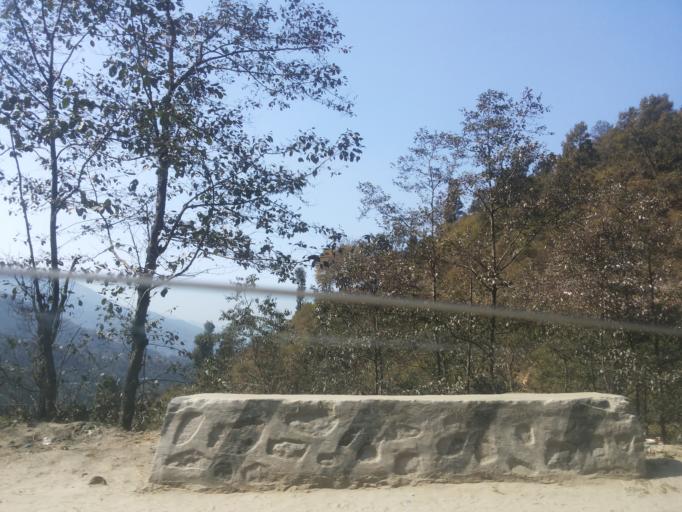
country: NP
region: Central Region
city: Kirtipur
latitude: 27.7112
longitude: 85.2023
